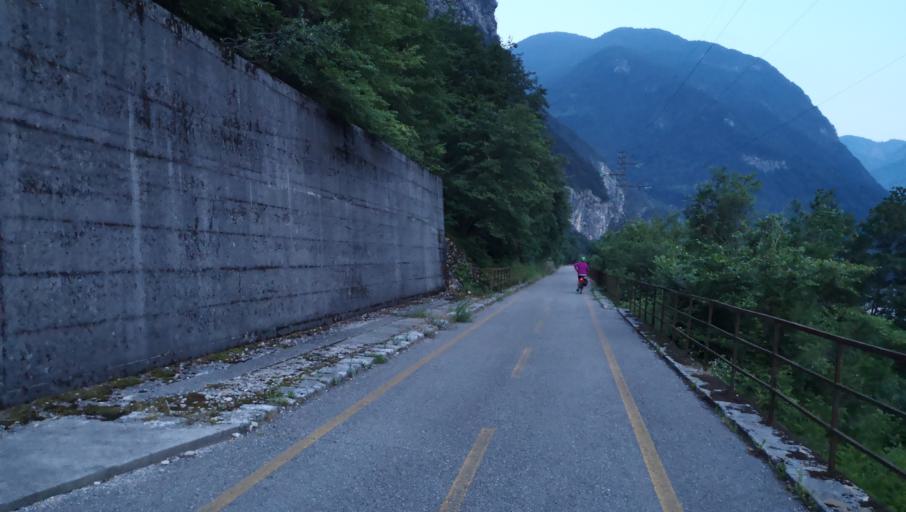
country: IT
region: Friuli Venezia Giulia
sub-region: Provincia di Udine
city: Dogna
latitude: 46.4275
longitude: 13.3179
